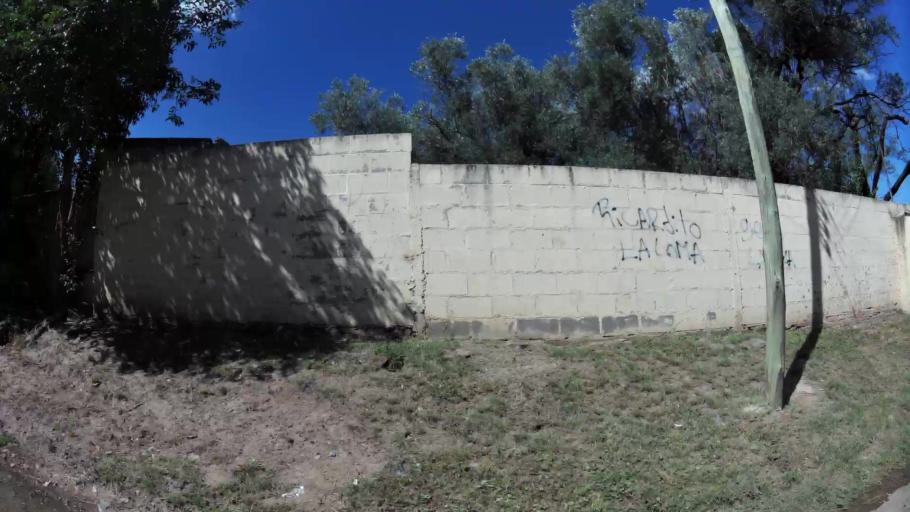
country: AR
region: Cordoba
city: Saldan
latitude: -31.2983
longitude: -64.3046
